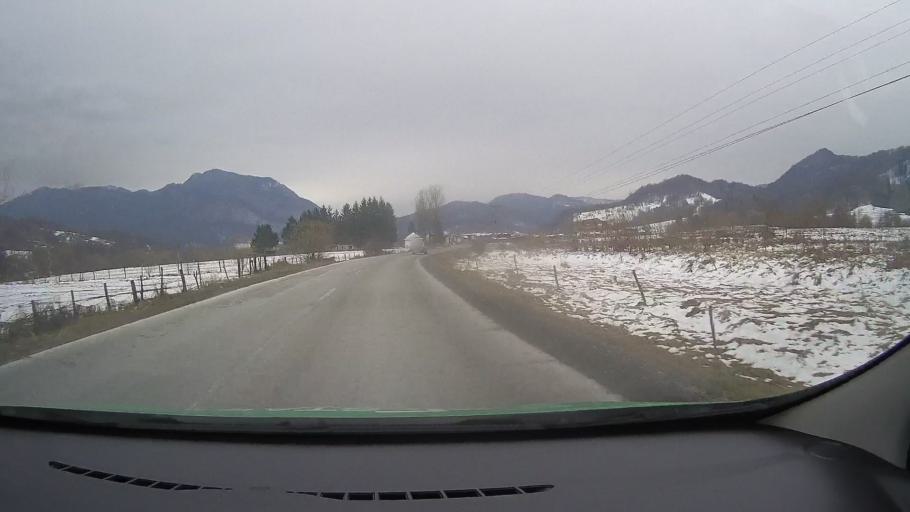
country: RO
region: Brasov
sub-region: Oras Rasnov
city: Rasnov
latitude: 45.5555
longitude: 25.4842
